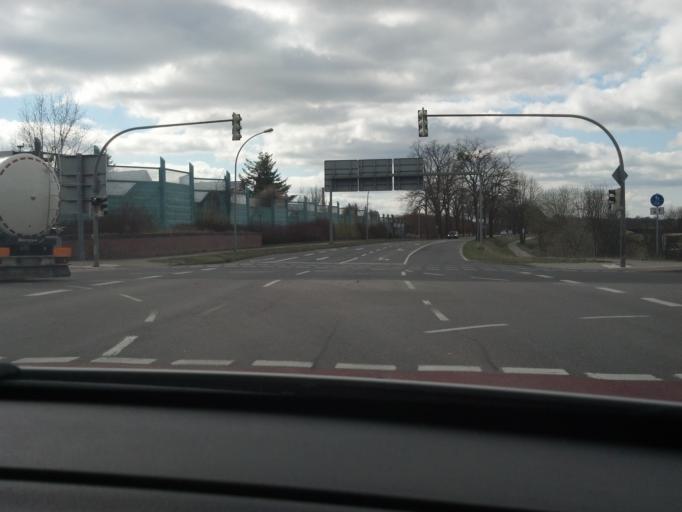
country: DE
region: Mecklenburg-Vorpommern
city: Neustrelitz
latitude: 53.3455
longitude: 13.1018
